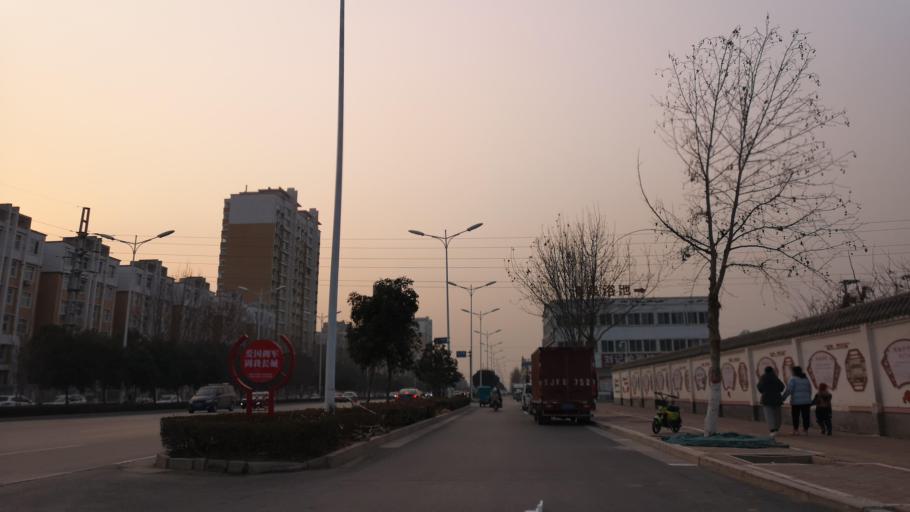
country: CN
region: Henan Sheng
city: Zhongyuanlu
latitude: 35.7892
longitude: 115.0896
